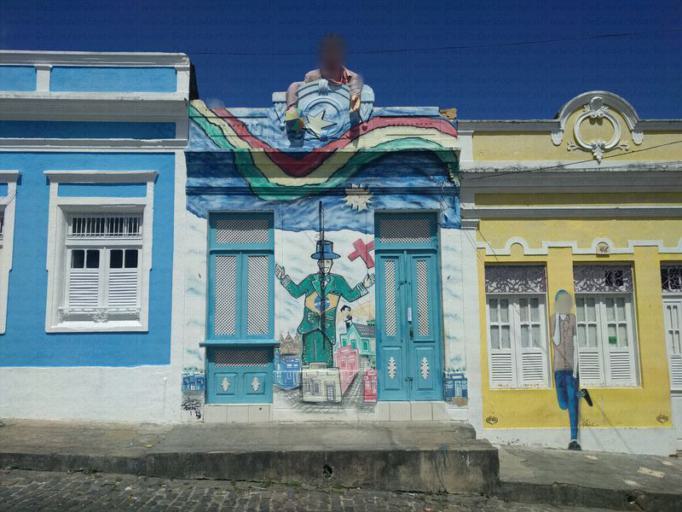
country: BR
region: Pernambuco
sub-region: Olinda
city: Olinda
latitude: -8.0143
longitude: -34.8527
